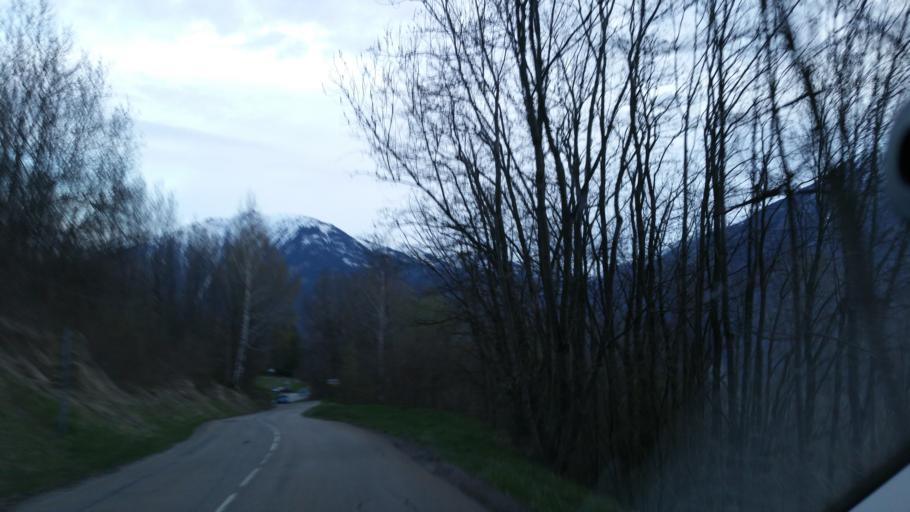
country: FR
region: Rhone-Alpes
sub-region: Departement de la Savoie
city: La Chambre
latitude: 45.3773
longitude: 6.3243
